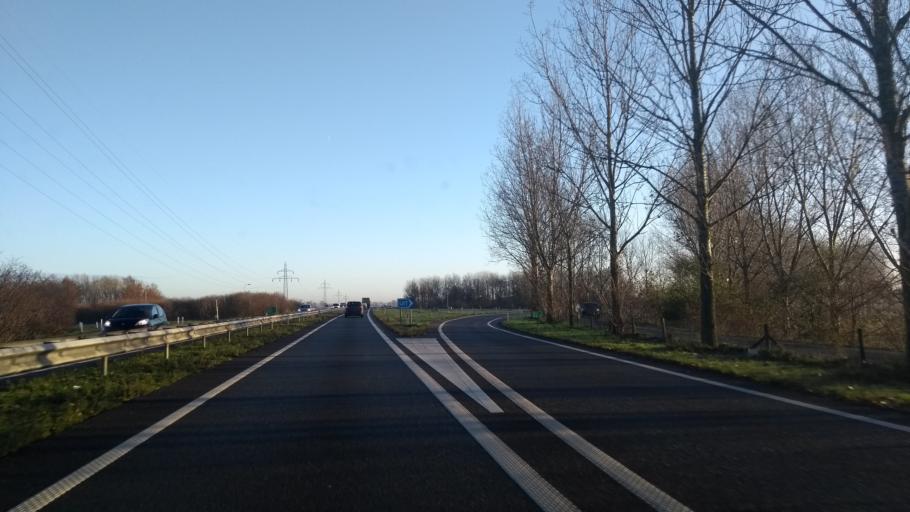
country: NL
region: Overijssel
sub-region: Gemeente Twenterand
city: Vriezenveen
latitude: 52.3875
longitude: 6.6177
